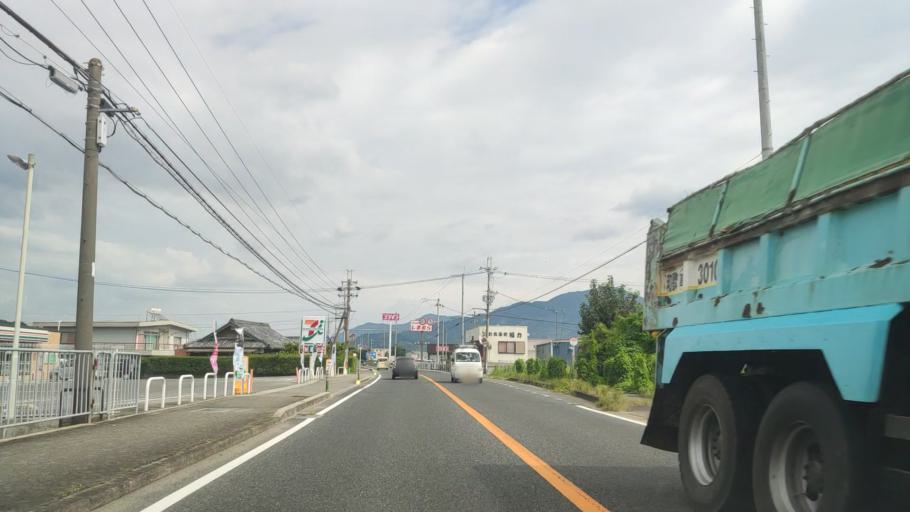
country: JP
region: Wakayama
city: Iwade
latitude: 34.2691
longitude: 135.4127
